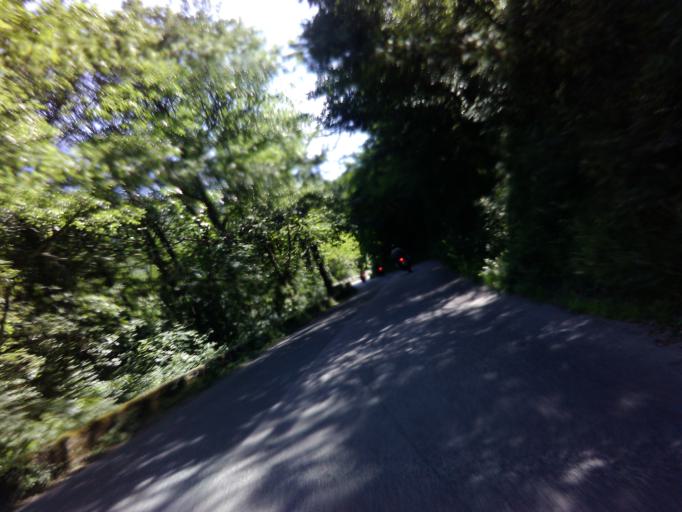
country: IT
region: Tuscany
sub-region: Provincia di Massa-Carrara
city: Licciana Nardi
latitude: 44.2855
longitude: 10.0786
